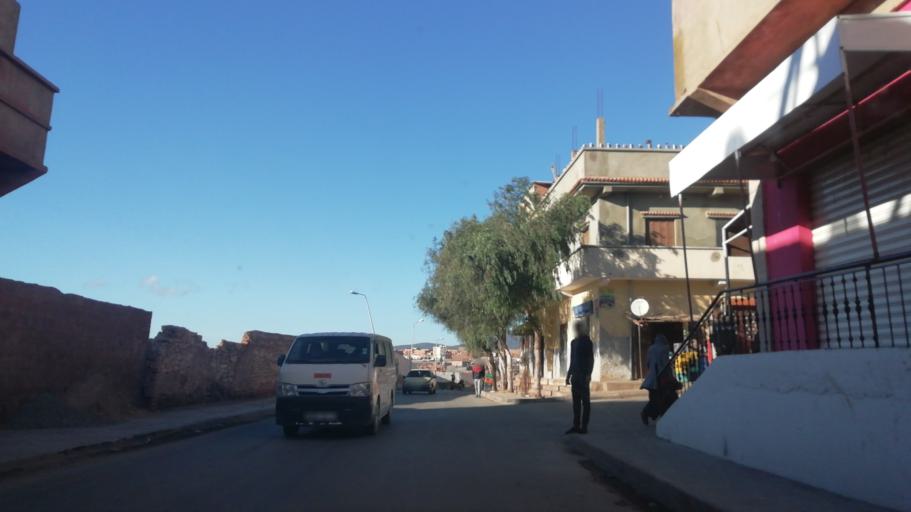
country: DZ
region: Oran
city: Sidi ech Chahmi
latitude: 35.6942
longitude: -0.4943
